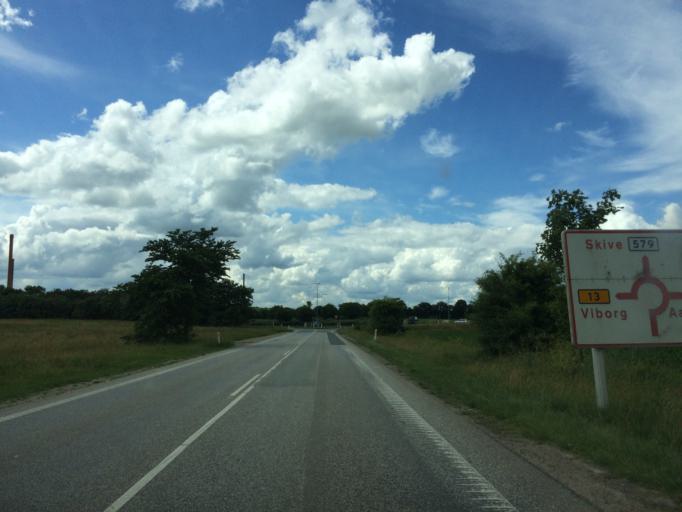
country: DK
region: North Denmark
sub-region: Vesthimmerland Kommune
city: Alestrup
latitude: 56.6212
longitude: 9.5145
